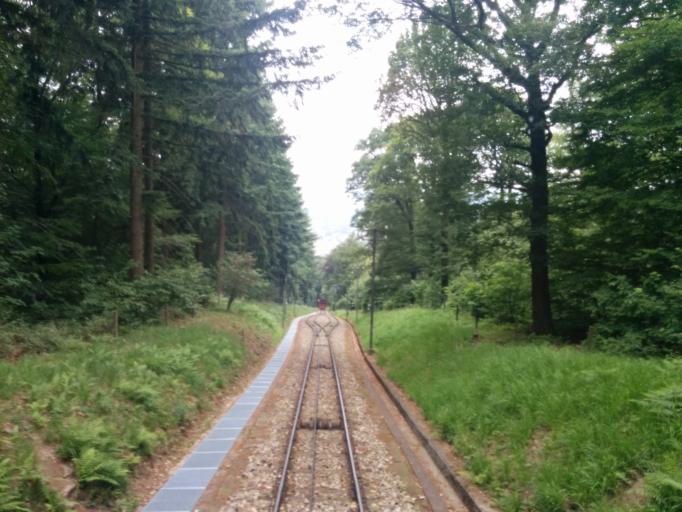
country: DE
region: Baden-Wuerttemberg
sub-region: Karlsruhe Region
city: Heidelberg
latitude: 49.4052
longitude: 8.7218
